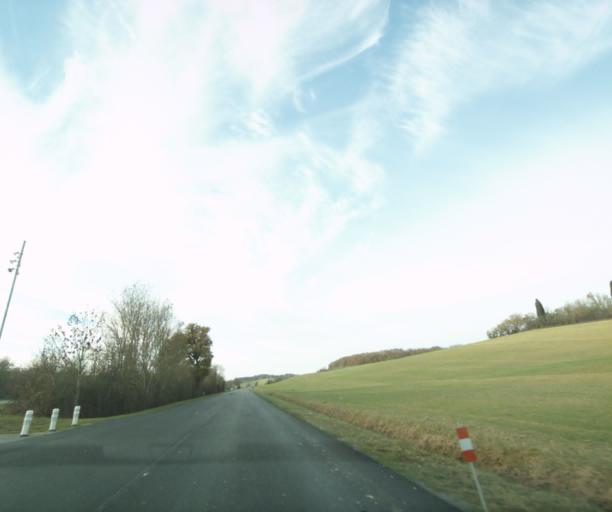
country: FR
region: Midi-Pyrenees
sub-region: Departement du Gers
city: Jegun
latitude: 43.6844
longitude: 0.4903
